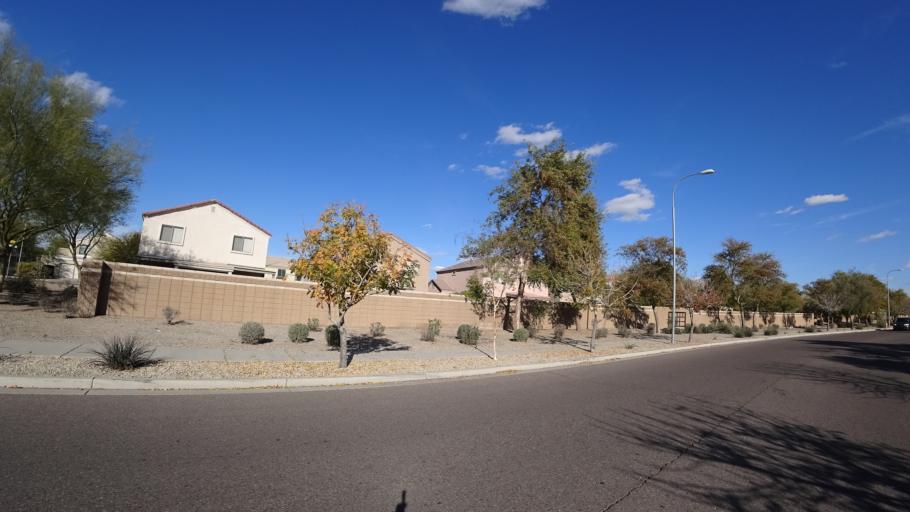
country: US
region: Arizona
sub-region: Maricopa County
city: Tolleson
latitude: 33.4197
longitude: -112.2451
